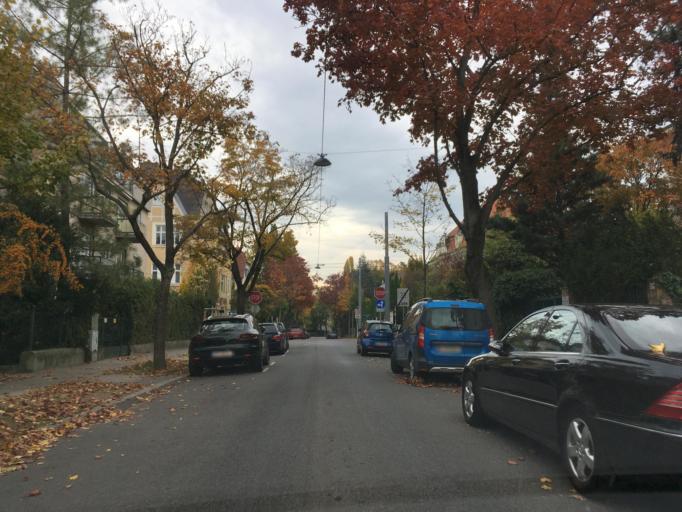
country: AT
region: Vienna
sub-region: Wien Stadt
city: Vienna
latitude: 48.2376
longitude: 16.3432
